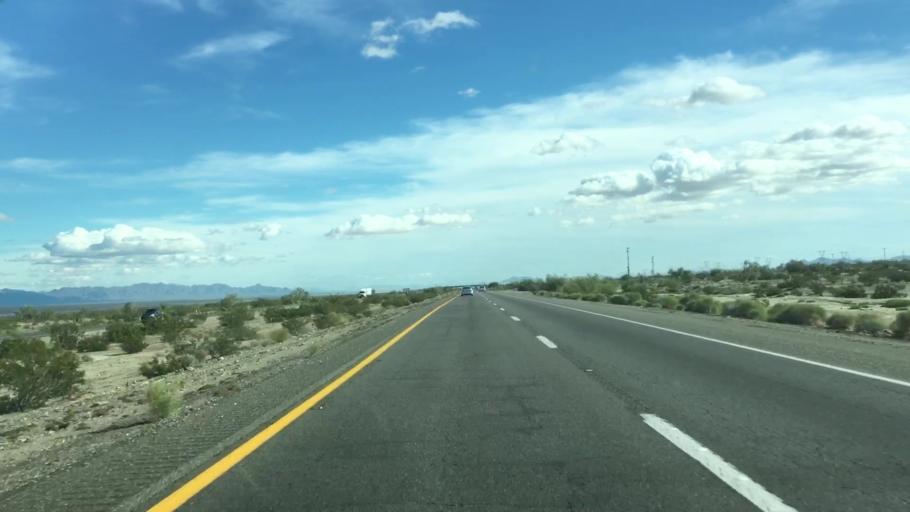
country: US
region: California
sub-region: Imperial County
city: Niland
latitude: 33.6875
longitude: -115.2607
